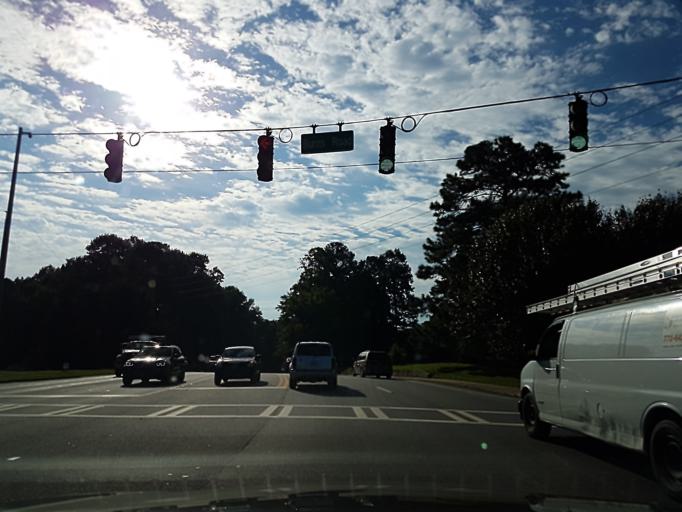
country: US
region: Georgia
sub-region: Gwinnett County
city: Lilburn
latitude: 33.9045
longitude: -84.1539
